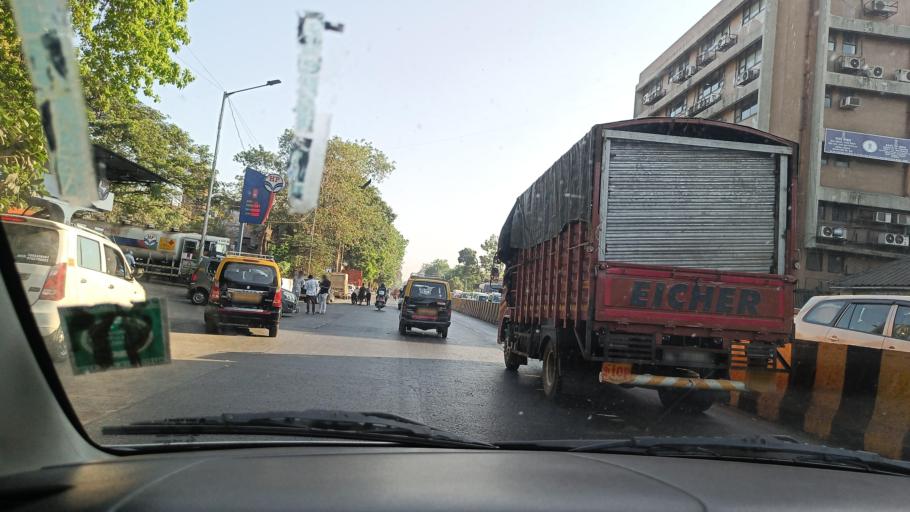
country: IN
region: Maharashtra
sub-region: Mumbai Suburban
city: Mumbai
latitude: 18.9562
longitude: 72.8424
